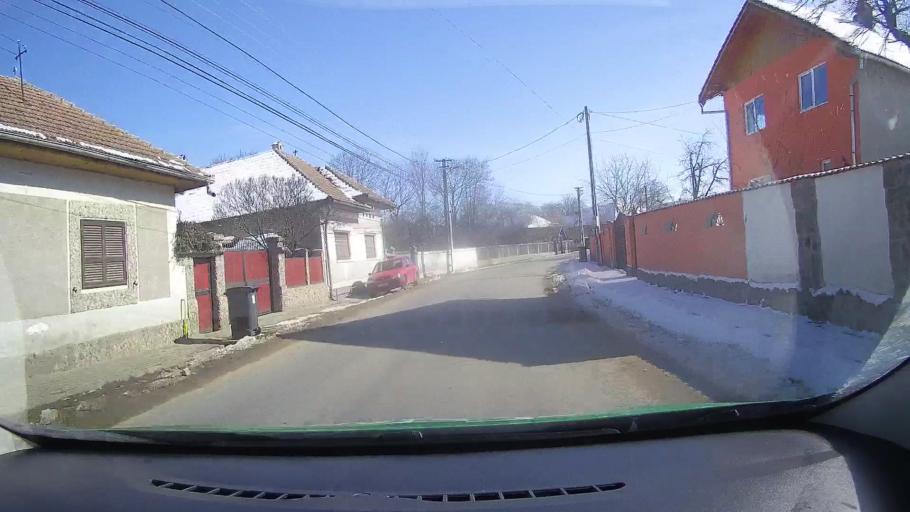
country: RO
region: Brasov
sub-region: Comuna Sambata de Sus
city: Sambata de Sus
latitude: 45.7613
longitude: 24.8215
